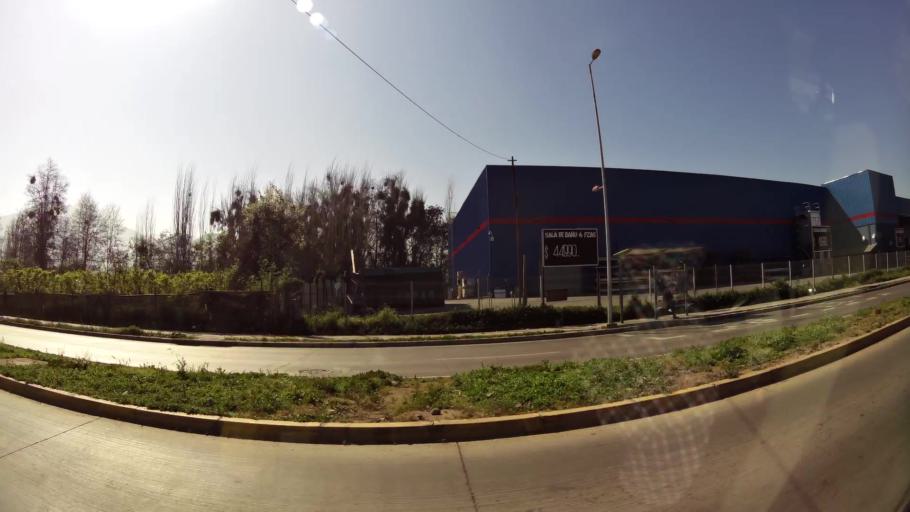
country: CL
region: Santiago Metropolitan
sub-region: Provincia de Chacabuco
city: Chicureo Abajo
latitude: -33.3693
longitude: -70.6710
